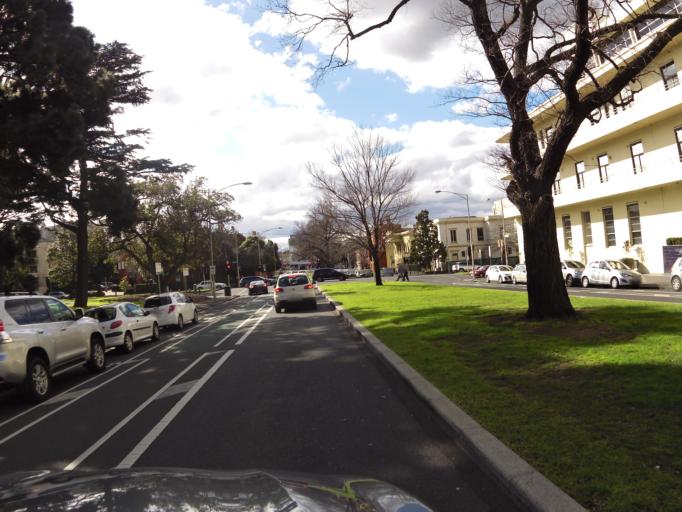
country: AU
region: Victoria
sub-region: Melbourne
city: East Melbourne
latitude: -37.8110
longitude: 144.9834
